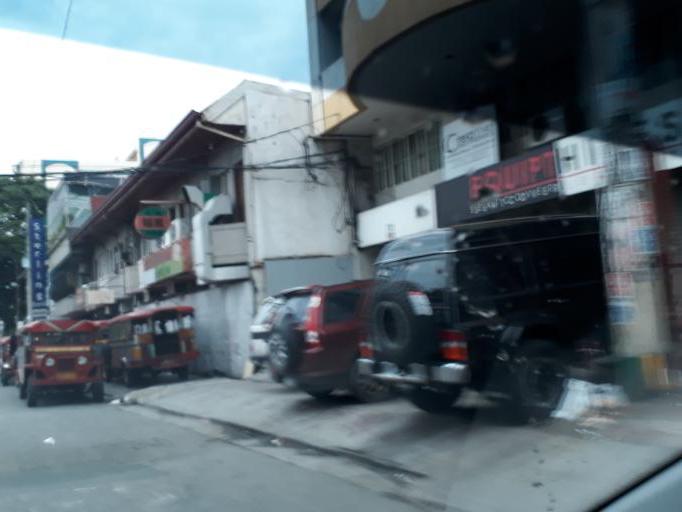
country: PH
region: Calabarzon
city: Del Monte
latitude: 14.6349
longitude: 121.0014
